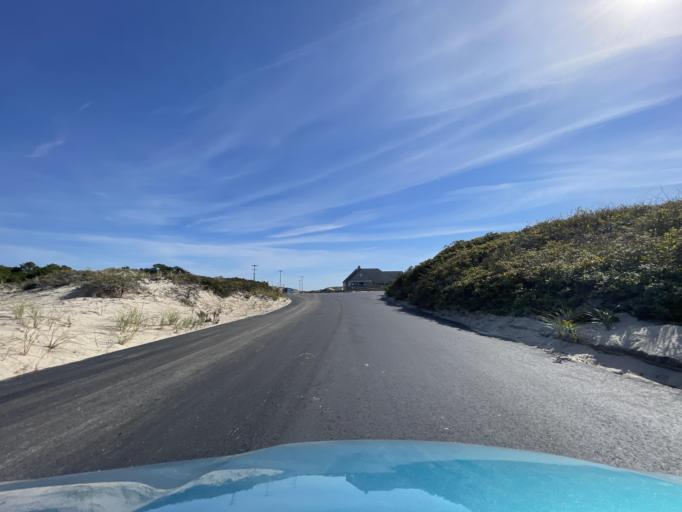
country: US
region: Massachusetts
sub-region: Bristol County
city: Head of Westport
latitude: 41.5071
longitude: -71.0551
